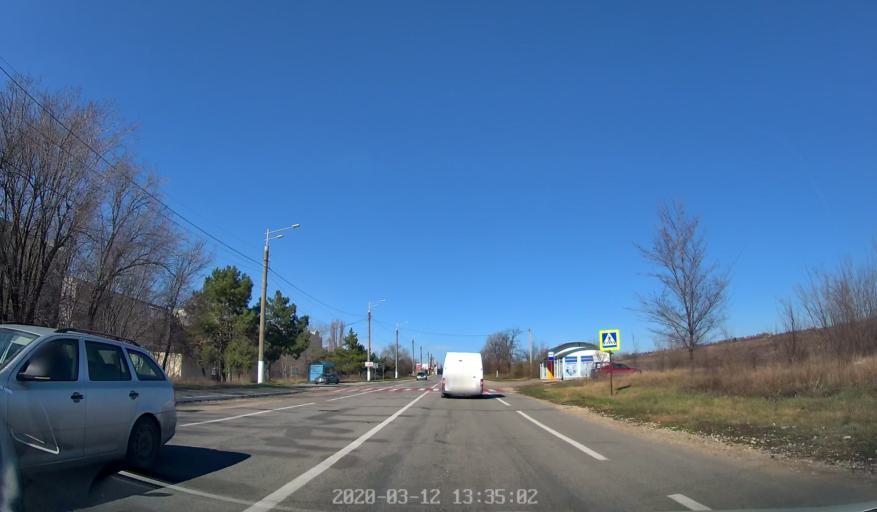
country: MD
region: Laloveni
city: Ialoveni
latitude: 46.9683
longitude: 28.7665
